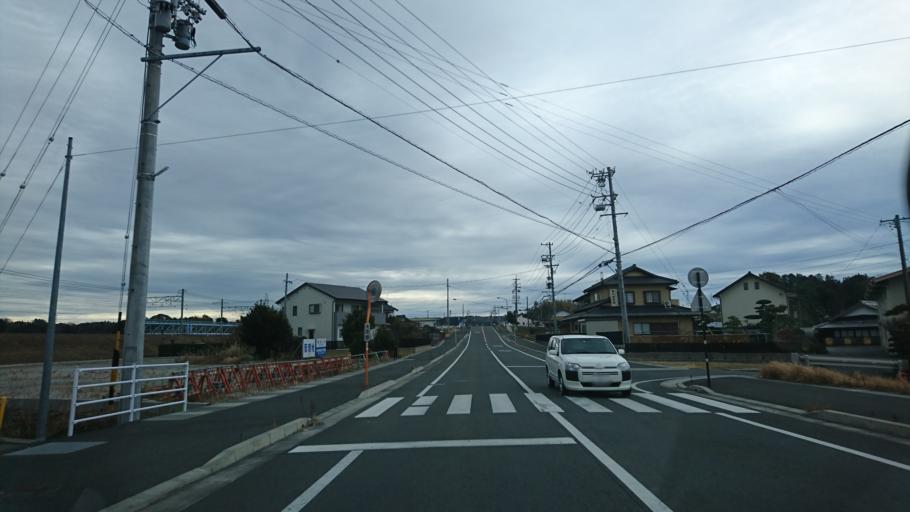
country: JP
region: Shizuoka
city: Kanaya
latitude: 34.7648
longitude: 138.0956
